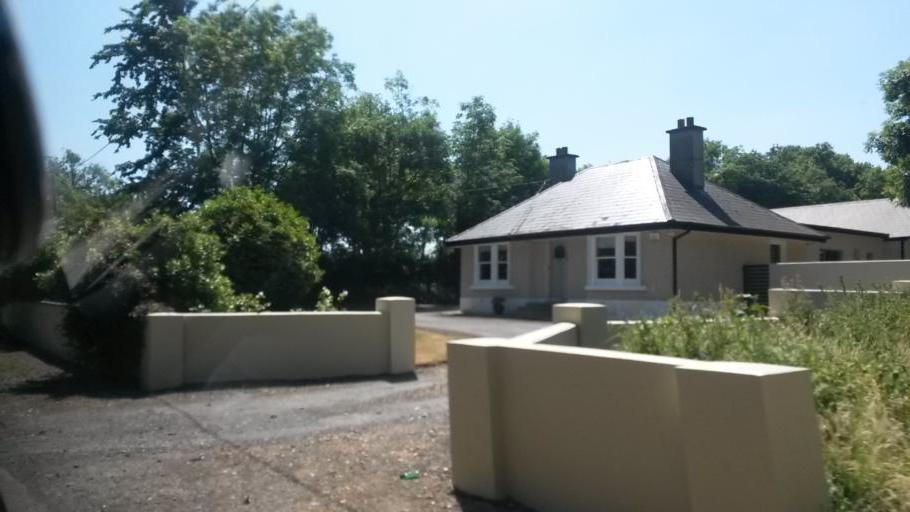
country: IE
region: Leinster
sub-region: An Mhi
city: Ashbourne
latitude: 53.5320
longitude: -6.3233
